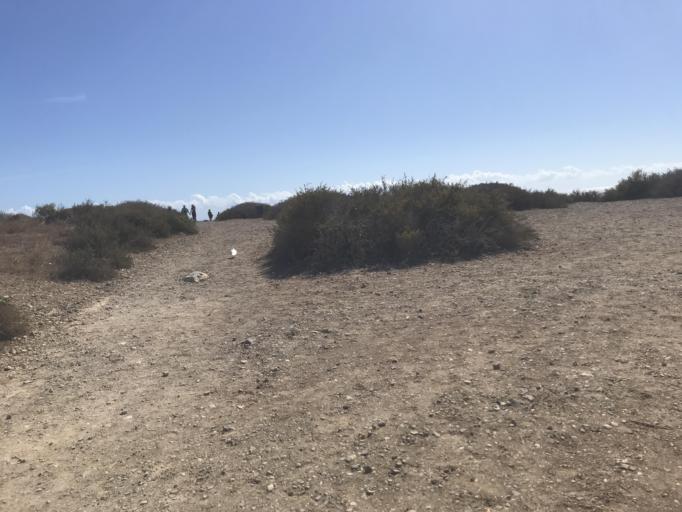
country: ES
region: Valencia
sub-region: Provincia de Alicante
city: Santa Pola
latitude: 38.1648
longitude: -0.4773
